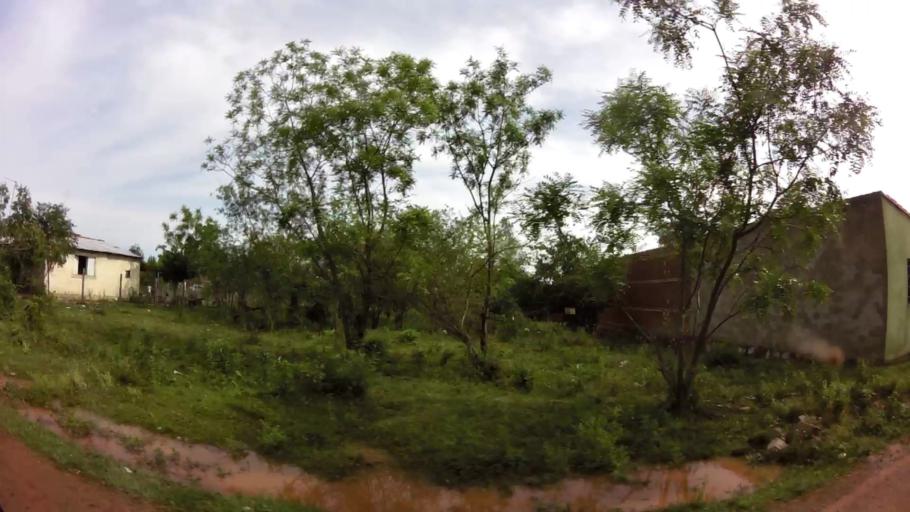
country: PY
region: Central
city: Limpio
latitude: -25.1223
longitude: -57.4771
